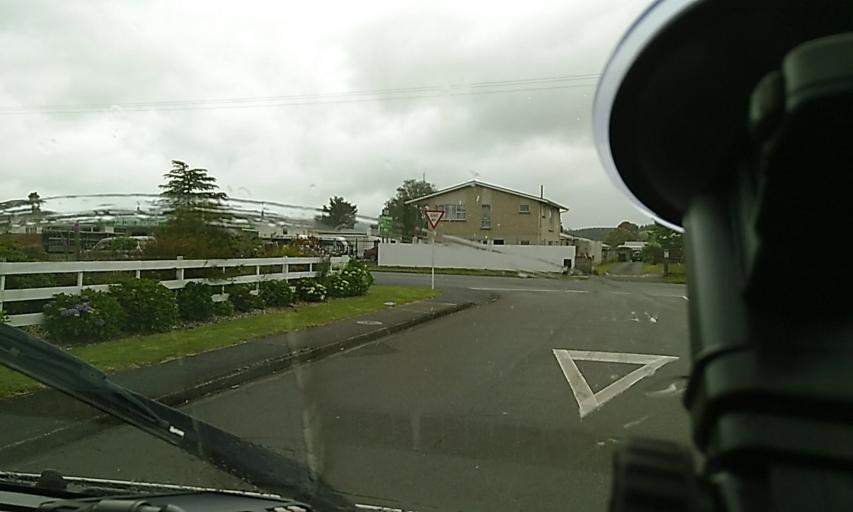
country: NZ
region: Northland
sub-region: Far North District
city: Waimate North
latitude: -35.4091
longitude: 173.8018
